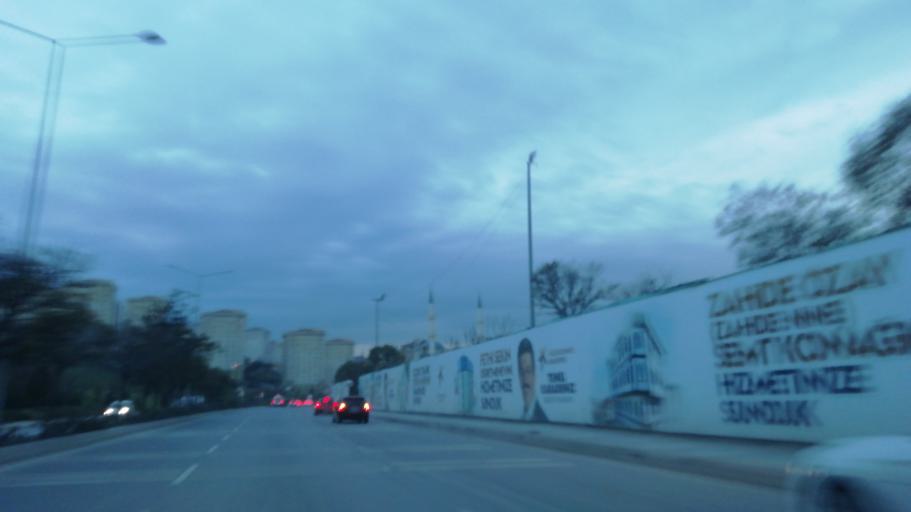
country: TR
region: Istanbul
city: Mahmutbey
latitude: 41.0427
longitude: 28.7736
